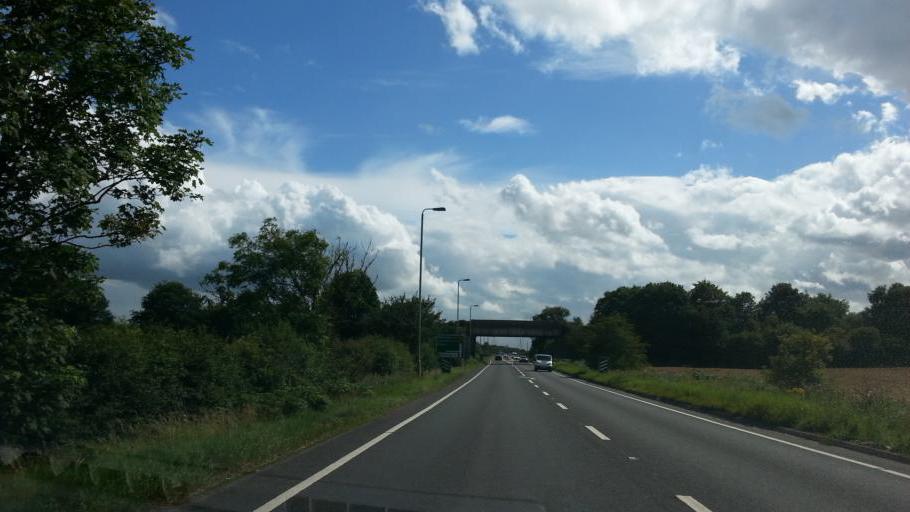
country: GB
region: England
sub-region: Nottinghamshire
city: Bilsthorpe
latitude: 53.1451
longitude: -1.0479
